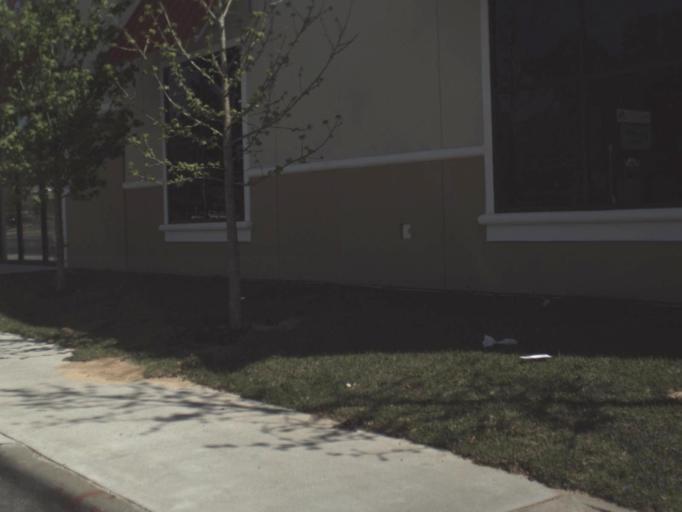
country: US
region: Florida
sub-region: Escambia County
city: Pensacola
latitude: 30.4200
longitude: -87.2266
